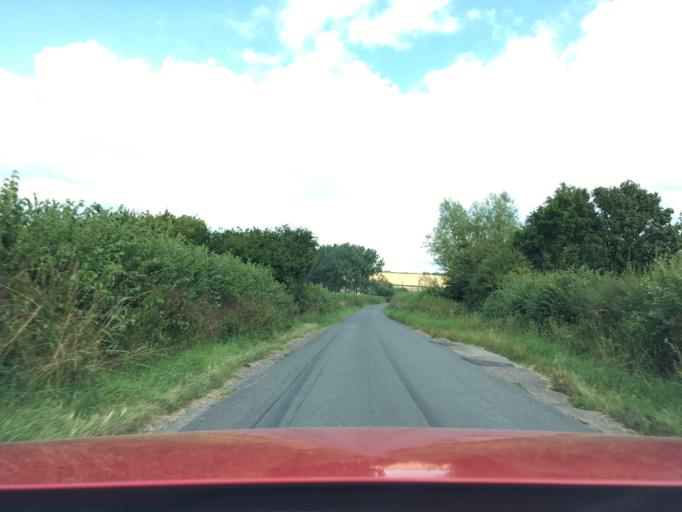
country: GB
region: England
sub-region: Gloucestershire
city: Gloucester
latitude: 51.9091
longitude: -2.2424
